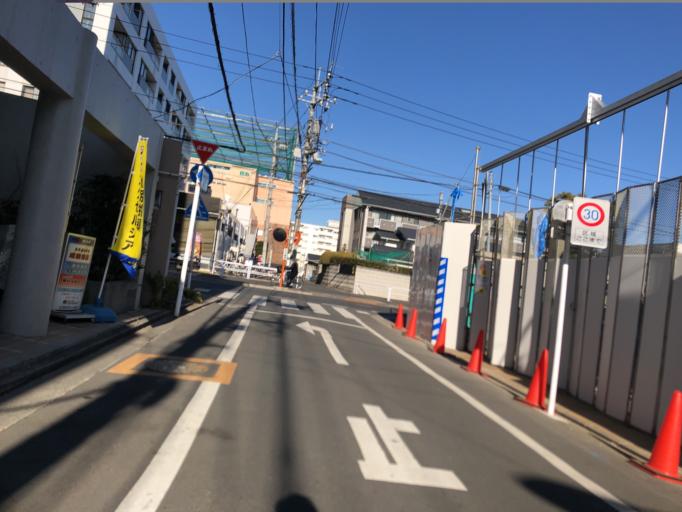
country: JP
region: Tokyo
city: Musashino
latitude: 35.7129
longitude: 139.5619
